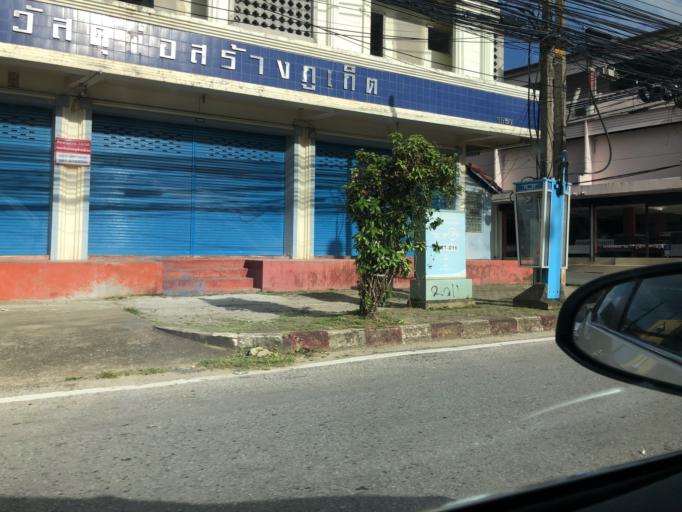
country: TH
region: Phuket
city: Ban Ratsada
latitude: 7.9199
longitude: 98.3957
